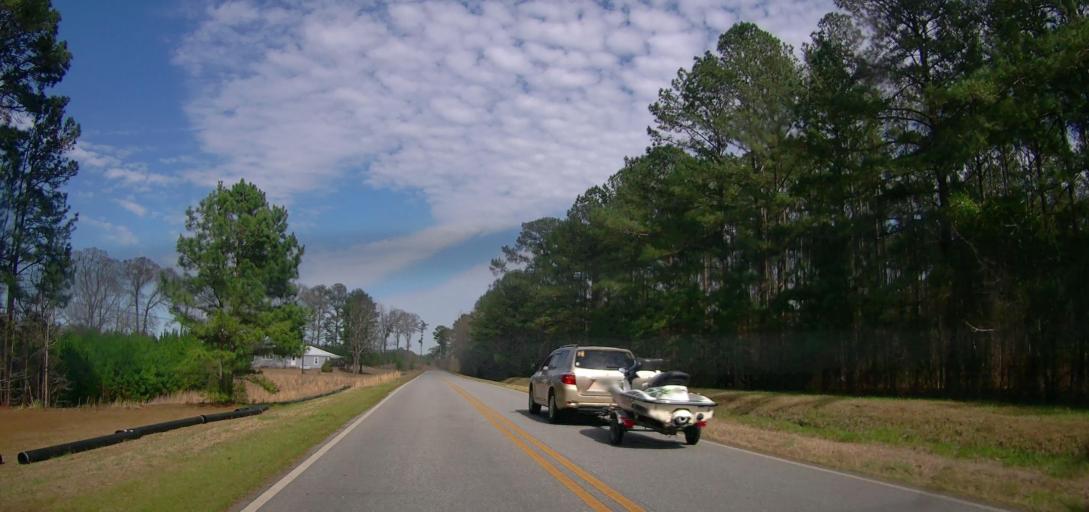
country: US
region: Georgia
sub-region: Monroe County
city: Forsyth
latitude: 33.1032
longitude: -83.8219
